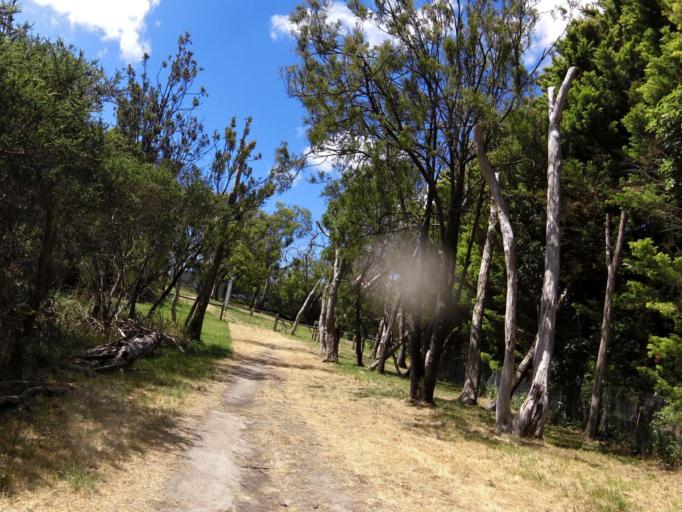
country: AU
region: Victoria
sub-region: Mornington Peninsula
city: Moorooduc
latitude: -38.2026
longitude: 145.1112
